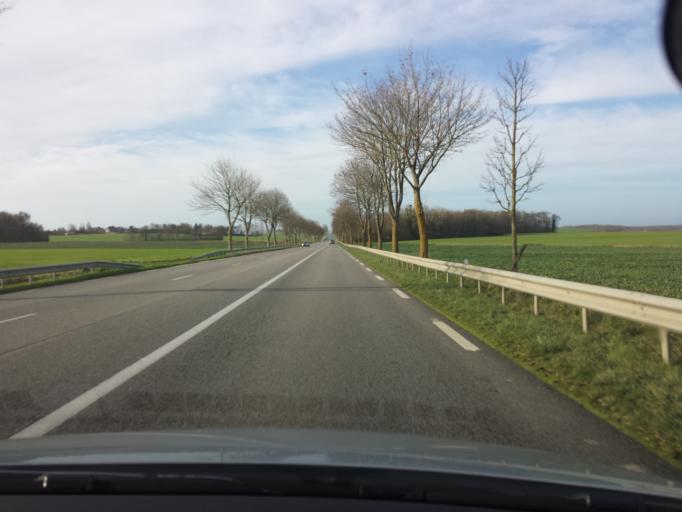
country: FR
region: Haute-Normandie
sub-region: Departement de l'Eure
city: Breuilpont
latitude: 49.0174
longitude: 1.4706
